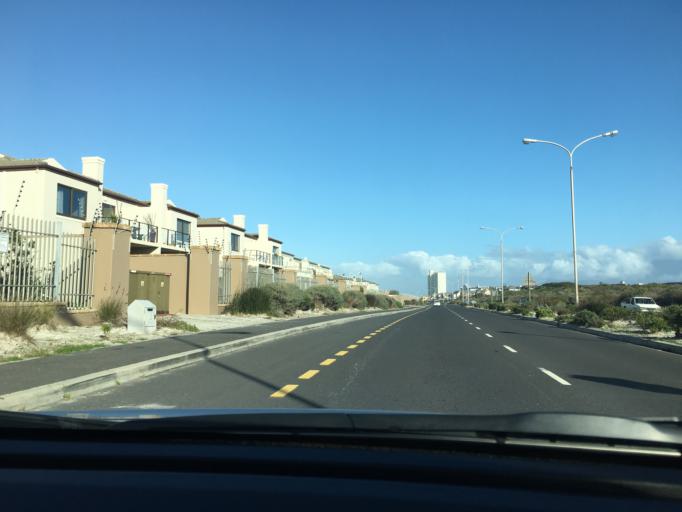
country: ZA
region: Western Cape
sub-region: City of Cape Town
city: Sunset Beach
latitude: -33.7951
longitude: 18.4617
